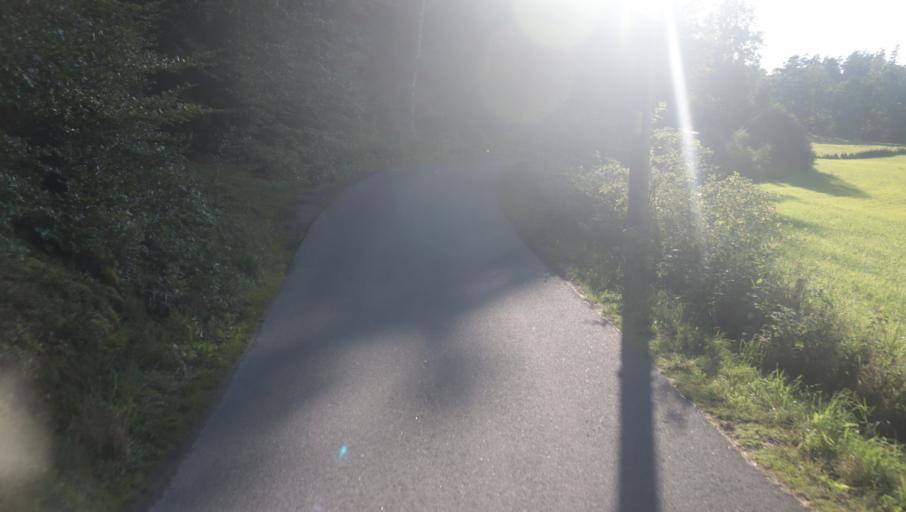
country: SE
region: Blekinge
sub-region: Karlshamns Kommun
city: Karlshamn
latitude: 56.1637
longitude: 14.9598
